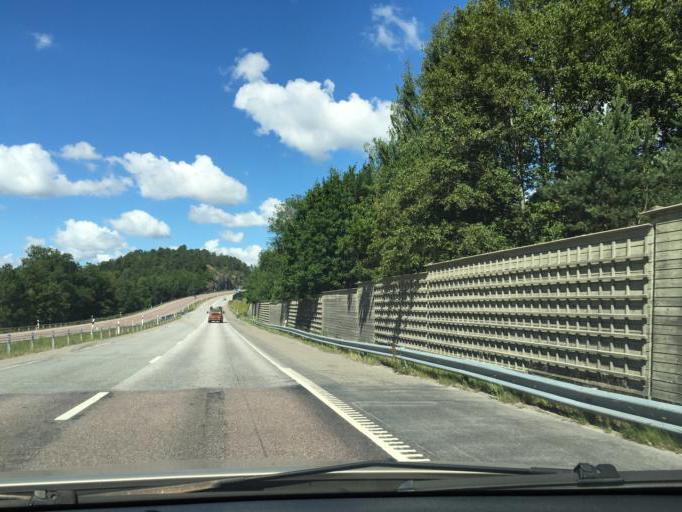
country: SE
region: Stockholm
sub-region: Nacka Kommun
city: Nacka
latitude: 59.3006
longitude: 18.1908
